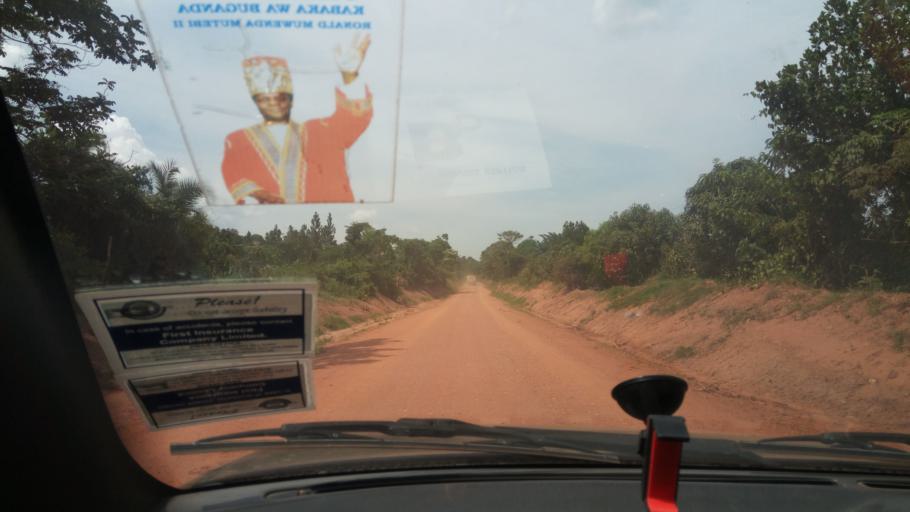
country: UG
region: Central Region
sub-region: Mityana District
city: Mityana
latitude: 0.4923
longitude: 32.1243
